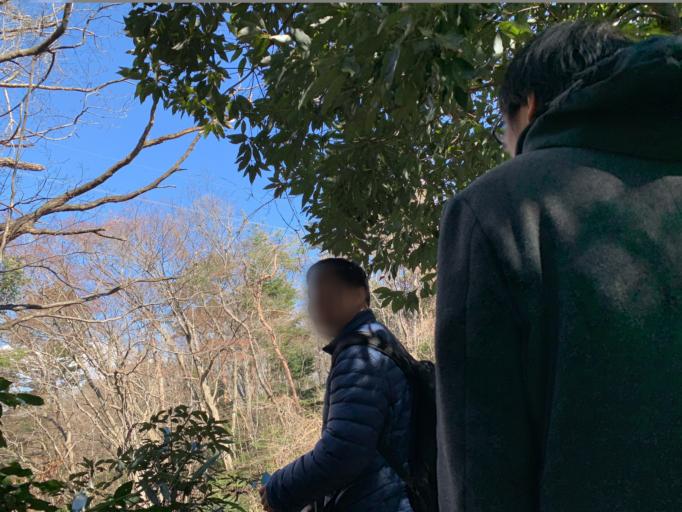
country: JP
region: Miyagi
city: Sendai
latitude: 38.2526
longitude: 140.8469
